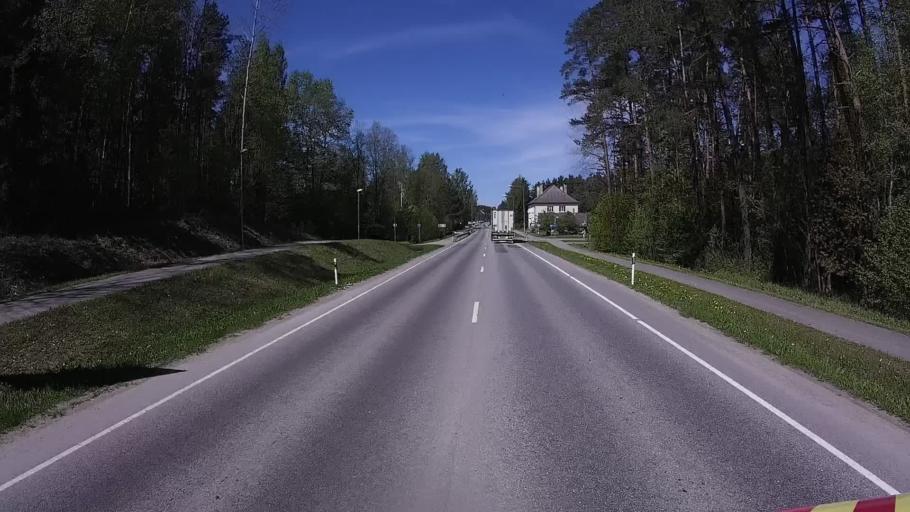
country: EE
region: Vorumaa
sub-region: Voru linn
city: Voru
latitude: 57.8187
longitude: 27.0251
